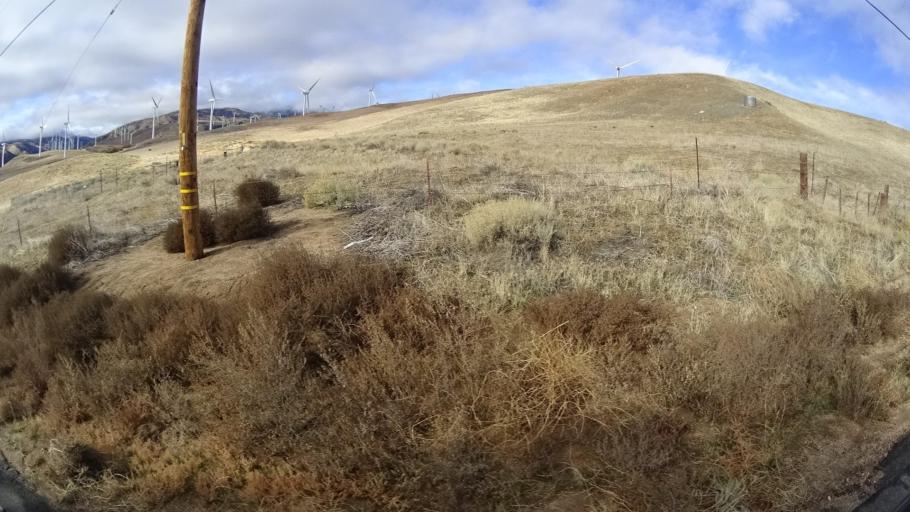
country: US
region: California
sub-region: Kern County
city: Tehachapi
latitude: 35.0654
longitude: -118.3530
